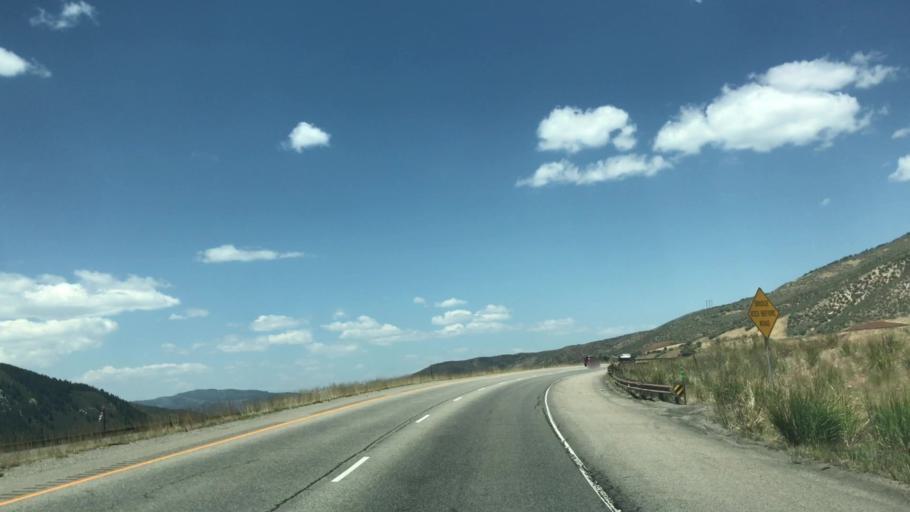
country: US
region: Colorado
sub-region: Eagle County
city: Avon
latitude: 39.6256
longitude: -106.4928
